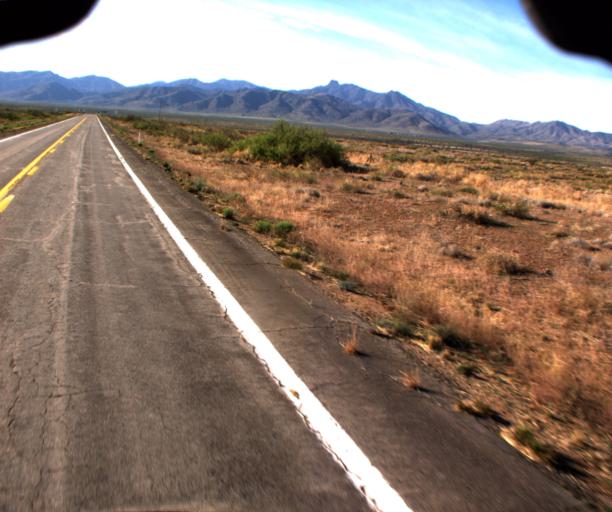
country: US
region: Arizona
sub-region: Cochise County
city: Willcox
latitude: 32.3680
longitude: -109.6241
